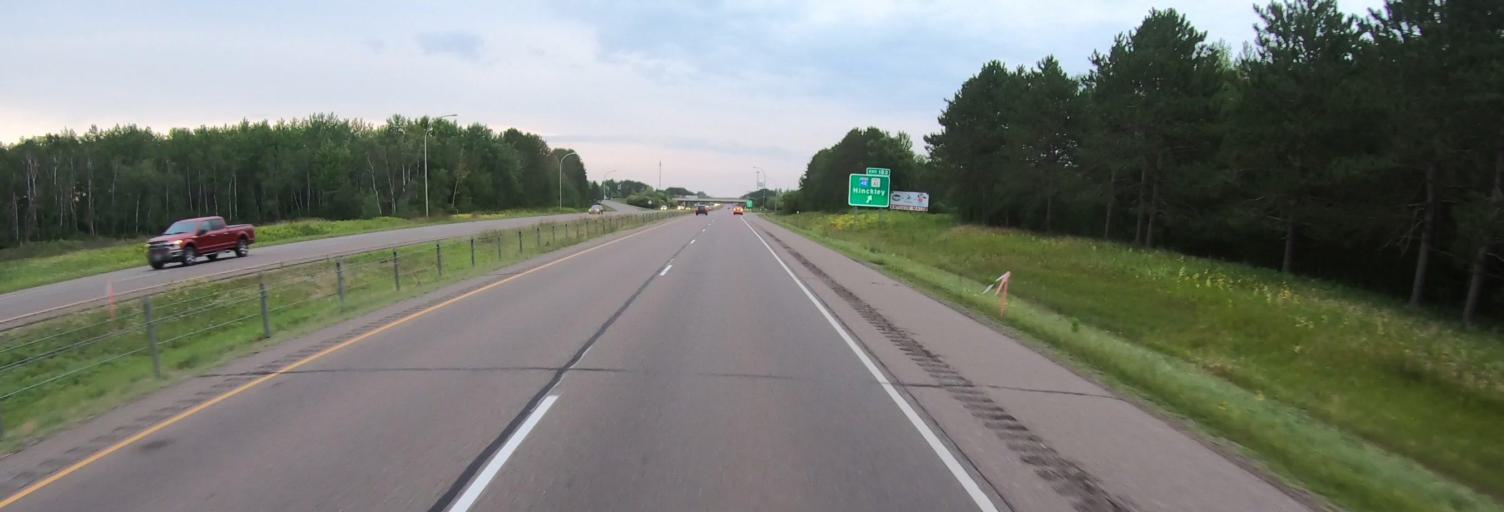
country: US
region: Minnesota
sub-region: Pine County
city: Hinckley
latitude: 46.0071
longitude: -92.9337
